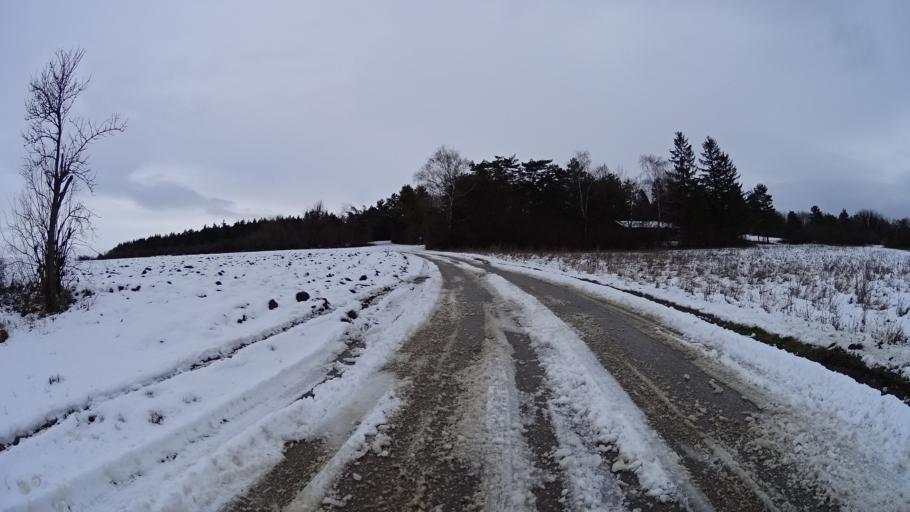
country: AT
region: Lower Austria
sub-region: Politischer Bezirk Korneuburg
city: Niederhollabrunn
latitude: 48.4243
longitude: 16.2876
